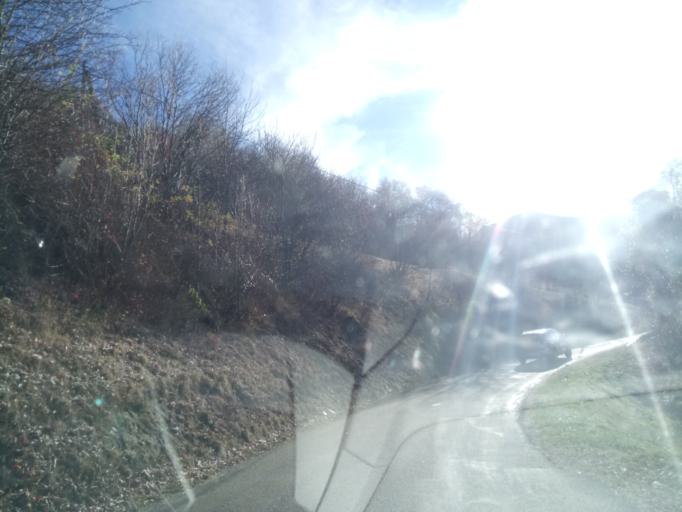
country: FR
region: Rhone-Alpes
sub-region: Departement de la Savoie
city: Saint-Michel-de-Maurienne
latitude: 45.2248
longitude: 6.4827
